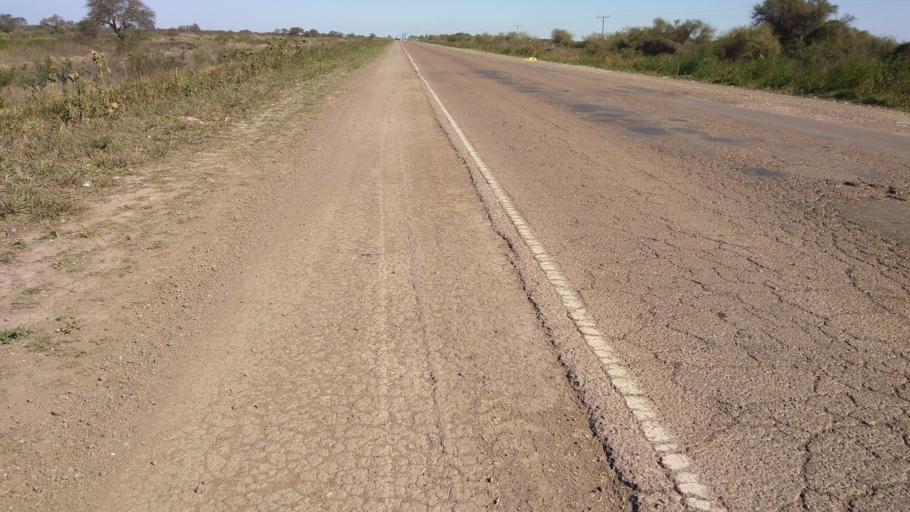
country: AR
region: Santiago del Estero
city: Los Juries
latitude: -28.6061
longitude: -61.5182
